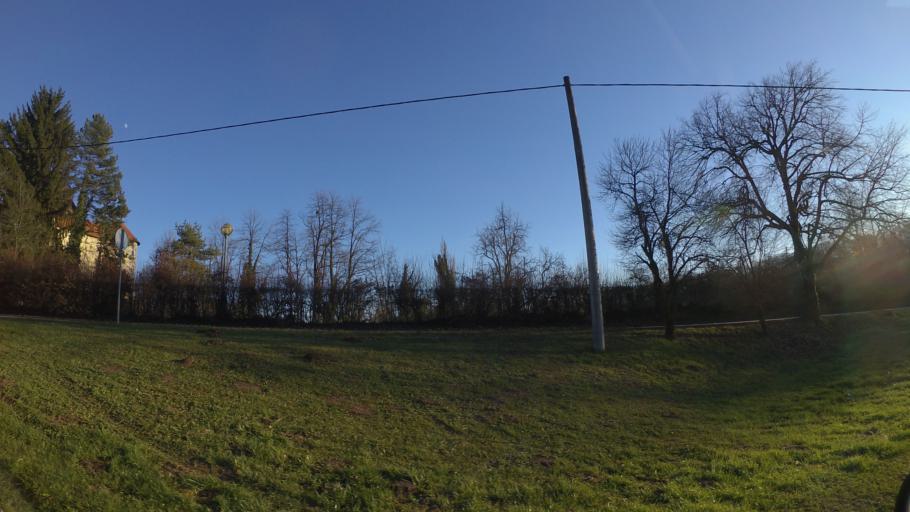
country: HR
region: Karlovacka
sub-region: Grad Karlovac
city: Karlovac
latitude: 45.4952
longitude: 15.5269
